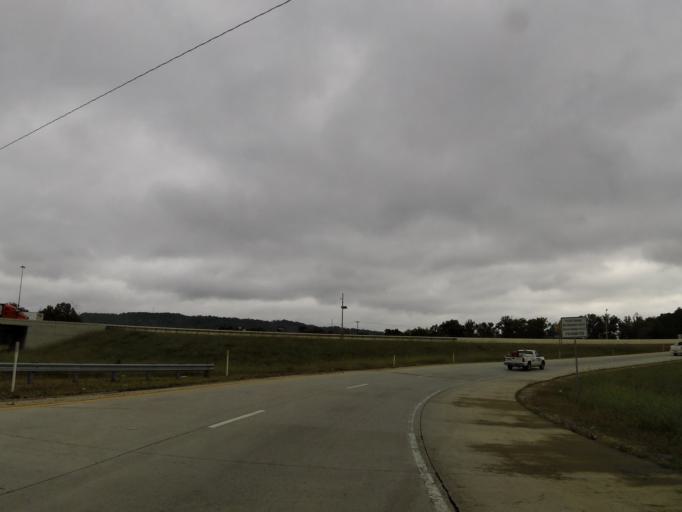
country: US
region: Tennessee
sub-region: Hamilton County
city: Collegedale
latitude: 35.0867
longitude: -85.0699
